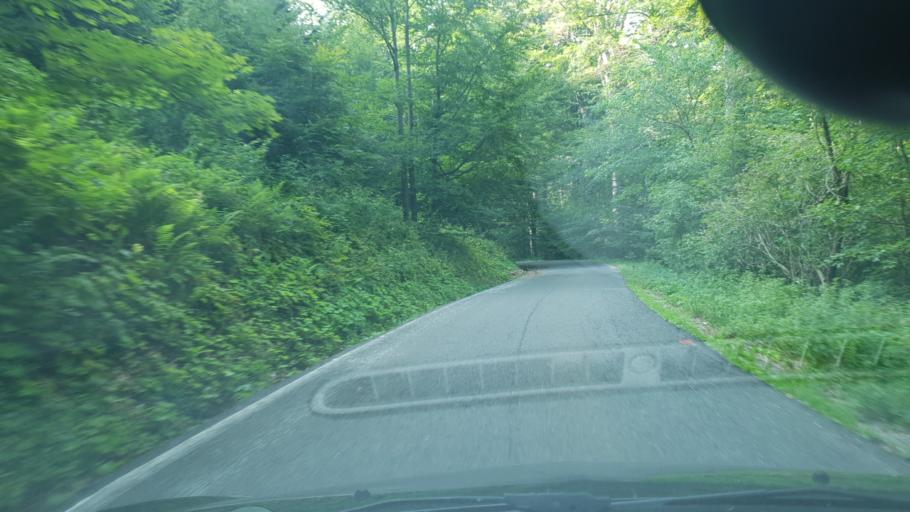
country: HR
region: Grad Zagreb
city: Kasina
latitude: 45.8967
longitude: 15.9527
